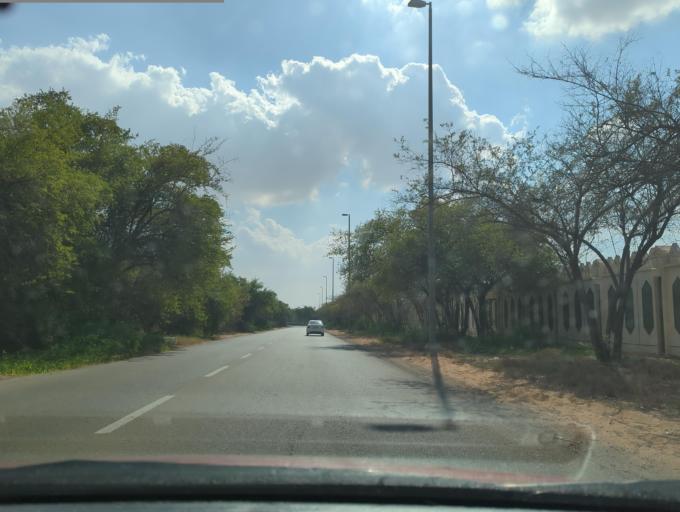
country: AE
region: Abu Dhabi
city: Al Ain
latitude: 24.1695
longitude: 55.6504
